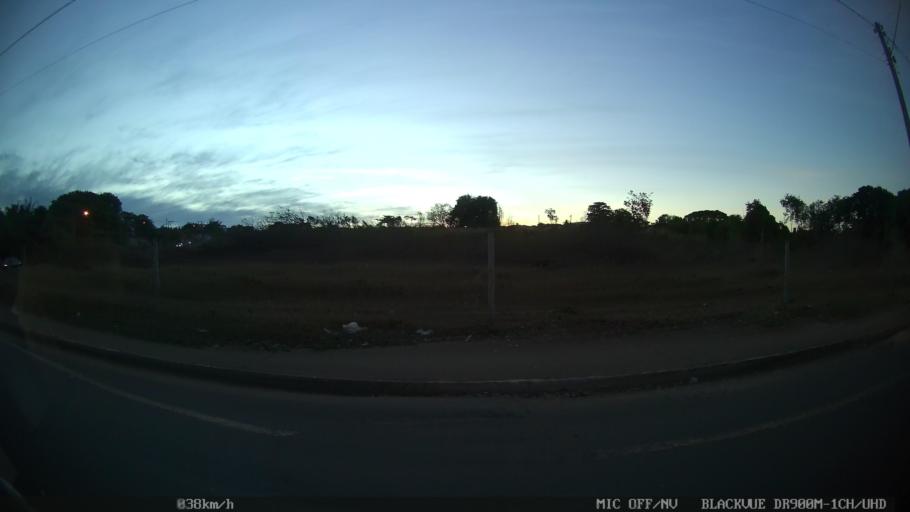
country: BR
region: Sao Paulo
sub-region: Catanduva
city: Catanduva
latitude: -21.1327
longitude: -48.9871
